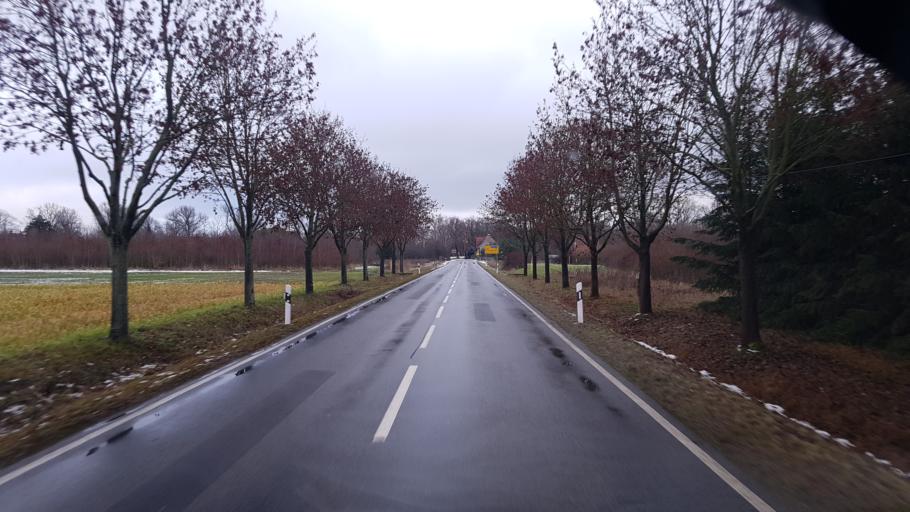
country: DE
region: Brandenburg
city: Schenkendobern
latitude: 51.8871
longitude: 14.6494
